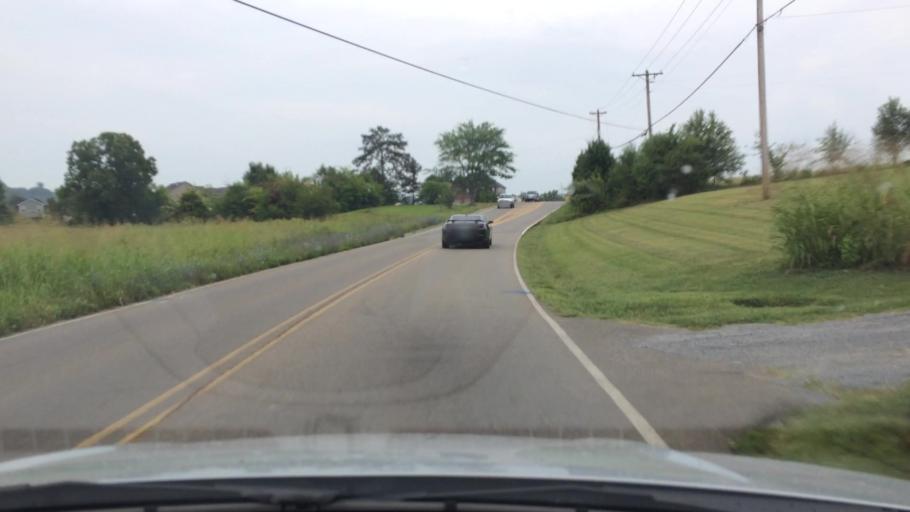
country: US
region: Tennessee
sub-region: Blount County
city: Maryville
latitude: 35.7389
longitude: -84.0144
